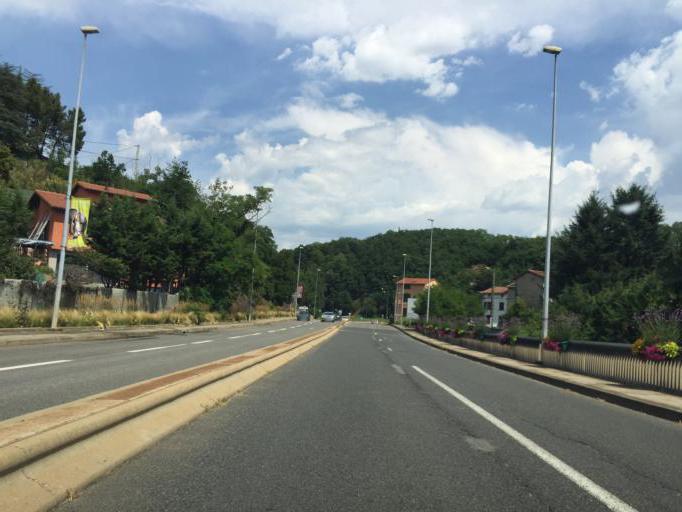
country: FR
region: Rhone-Alpes
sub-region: Departement du Rhone
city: Saint-Germain-Nuelles
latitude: 45.8372
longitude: 4.6191
